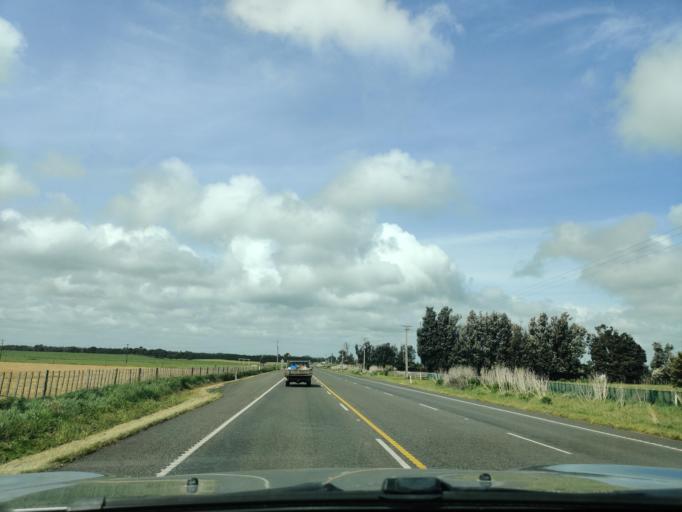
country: NZ
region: Taranaki
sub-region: South Taranaki District
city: Patea
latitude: -39.7668
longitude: 174.6088
